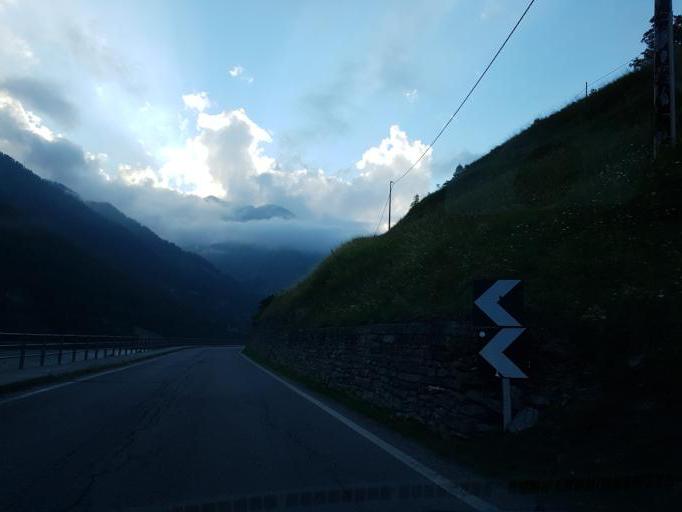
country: IT
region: Piedmont
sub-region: Provincia di Cuneo
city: Pontechianale
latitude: 44.6156
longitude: 7.0474
